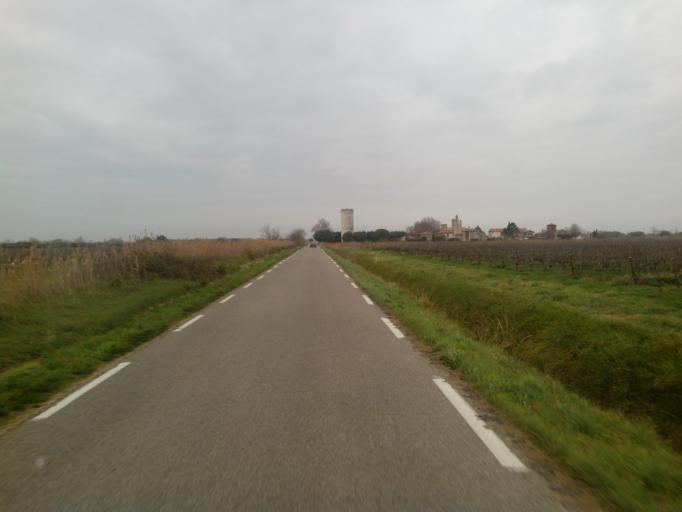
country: FR
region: Languedoc-Roussillon
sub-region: Departement du Gard
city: Aigues-Mortes
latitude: 43.5693
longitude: 4.3202
